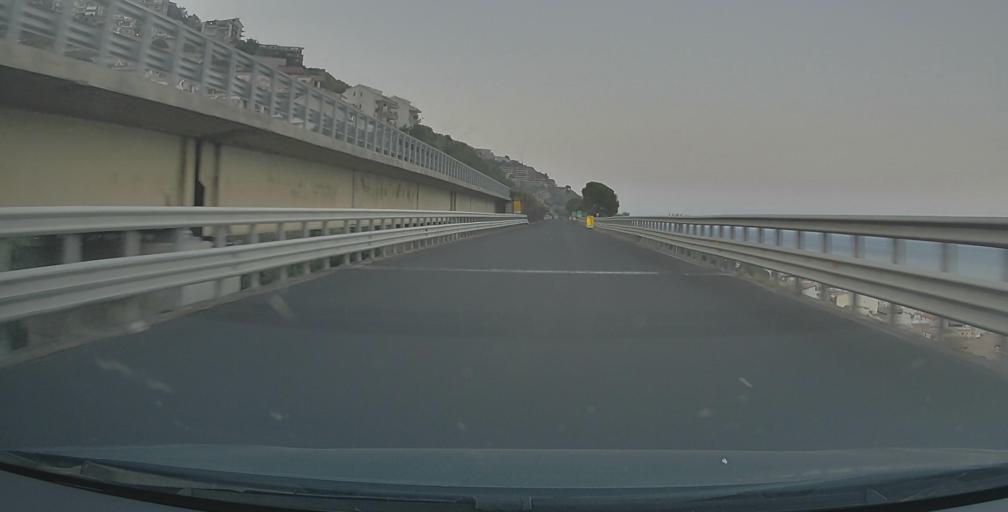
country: IT
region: Sicily
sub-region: Messina
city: Letojanni
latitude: 37.8835
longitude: 15.3086
